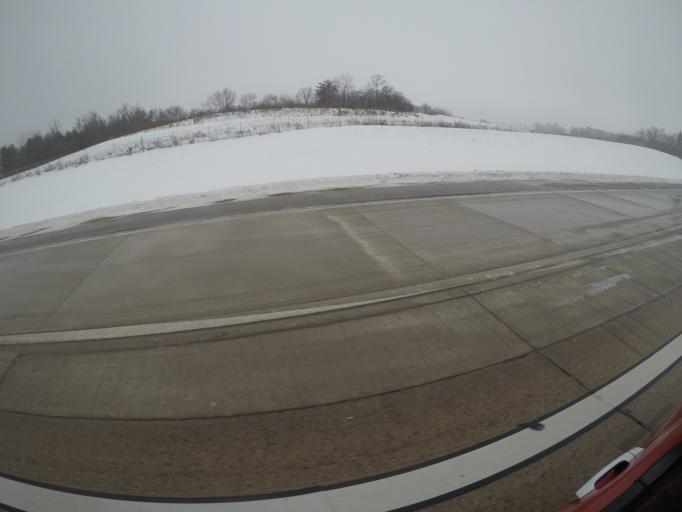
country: US
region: Minnesota
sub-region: Olmsted County
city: Oronoco
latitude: 44.1801
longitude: -92.5720
